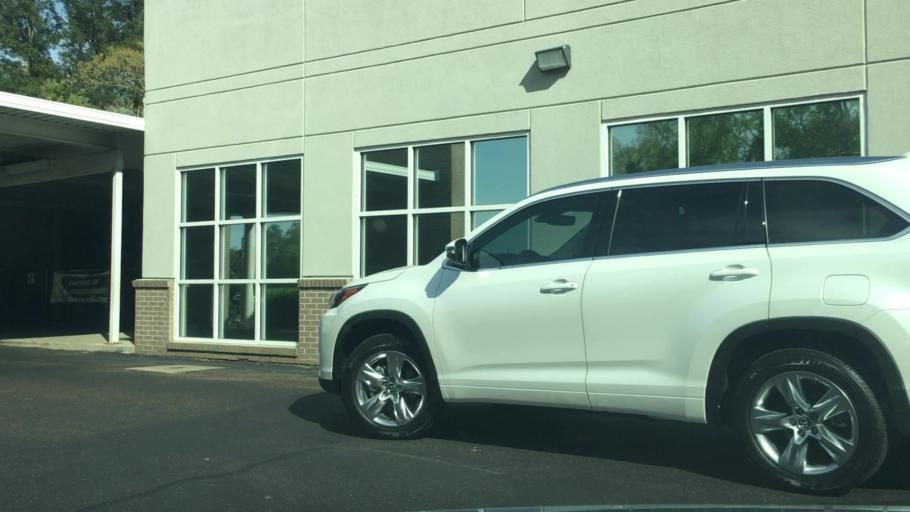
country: US
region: Mississippi
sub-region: Rankin County
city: Brandon
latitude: 32.3653
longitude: -89.9865
